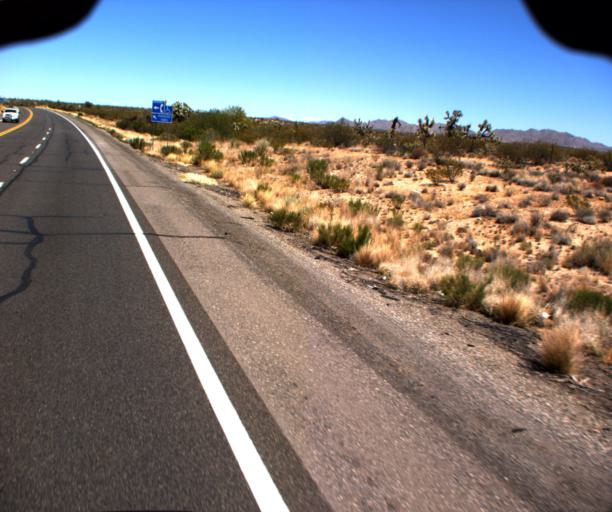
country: US
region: Arizona
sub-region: Yavapai County
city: Congress
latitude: 34.2256
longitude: -113.0694
